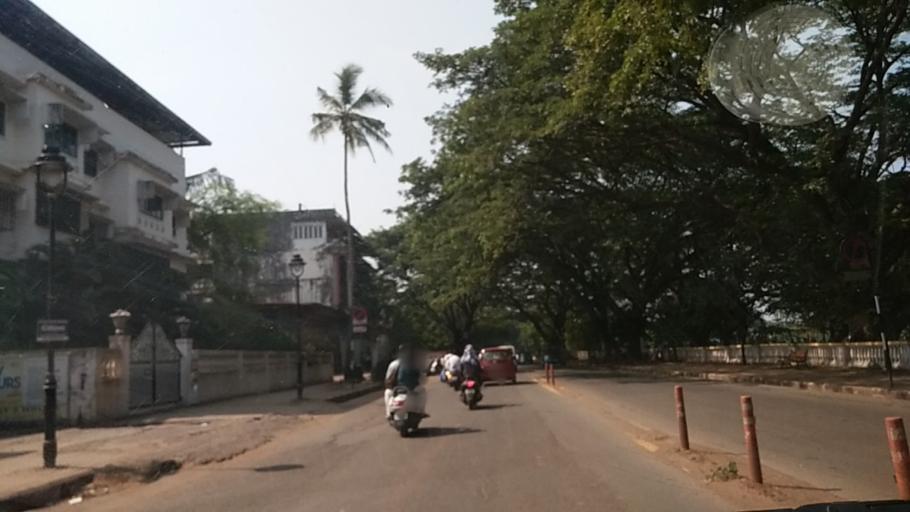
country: IN
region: Goa
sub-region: North Goa
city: Panaji
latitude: 15.4915
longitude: 73.8165
